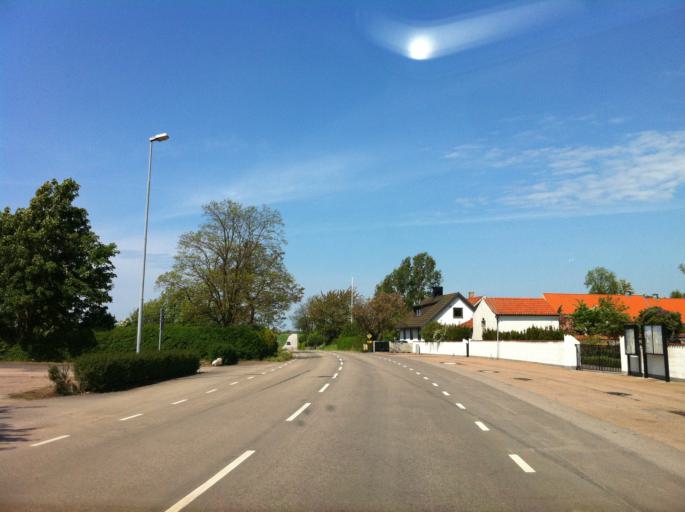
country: SE
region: Skane
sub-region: Helsingborg
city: Glumslov
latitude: 55.9189
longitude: 12.8610
